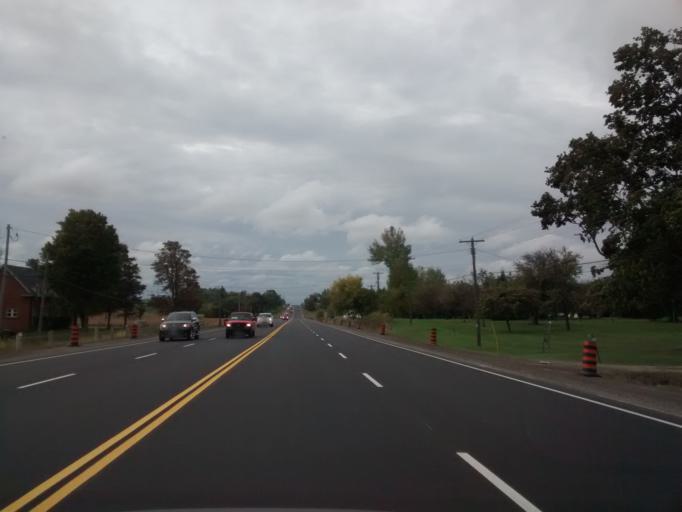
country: CA
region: Ontario
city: Ancaster
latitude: 43.1032
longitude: -79.9385
